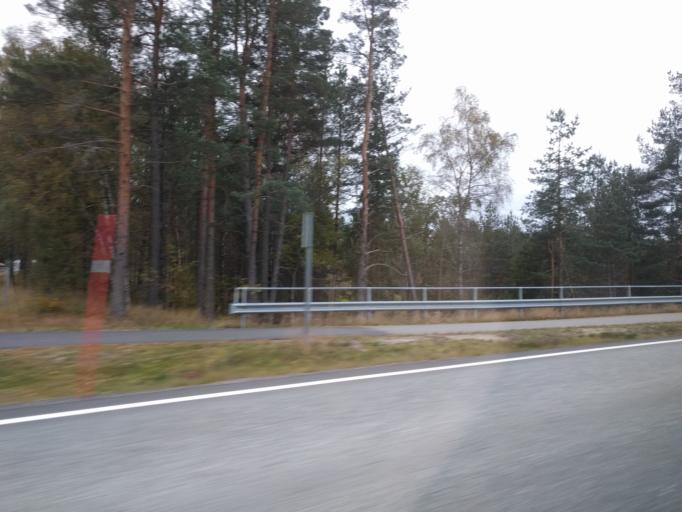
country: NO
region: Aust-Agder
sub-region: Evje og Hornnes
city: Evje
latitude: 58.5820
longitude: 7.7959
